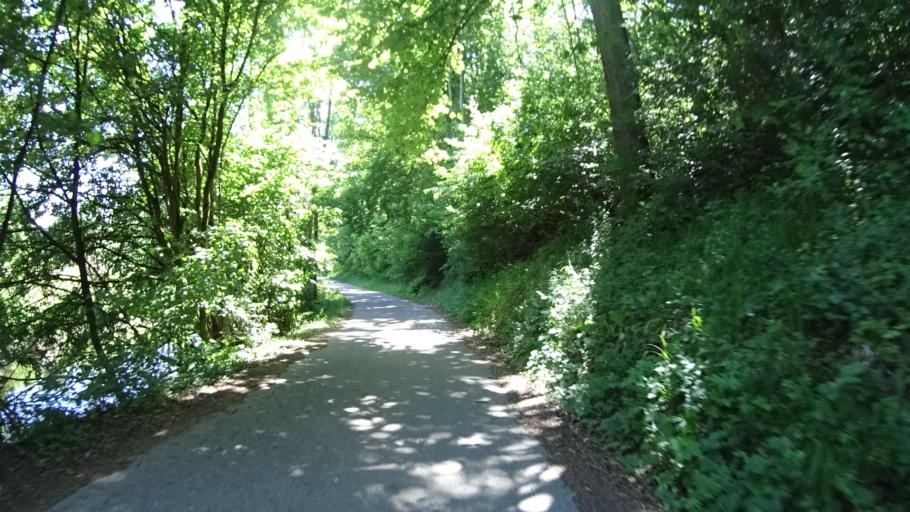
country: DE
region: Bavaria
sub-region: Regierungsbezirk Mittelfranken
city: Adelshofen
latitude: 49.4103
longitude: 10.1515
